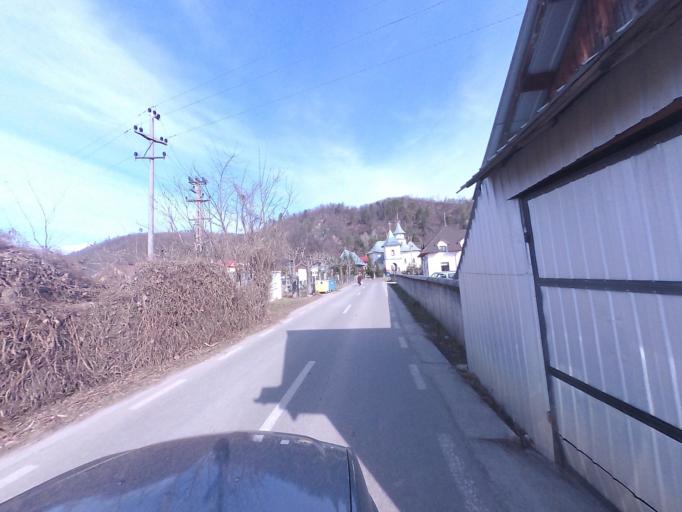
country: RO
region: Neamt
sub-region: Oras Targu Neamt
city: Humulesti
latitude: 47.2076
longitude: 26.3539
